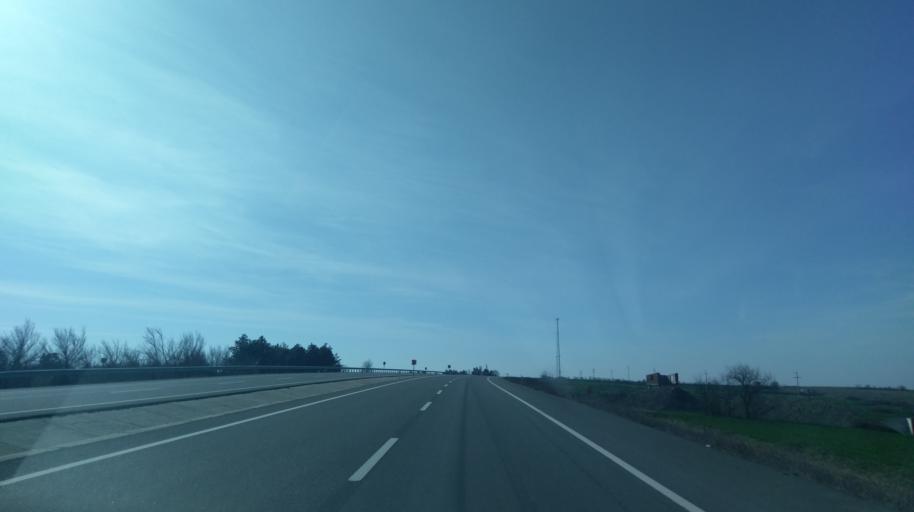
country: TR
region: Edirne
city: Hamidiye
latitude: 41.0825
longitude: 26.6398
